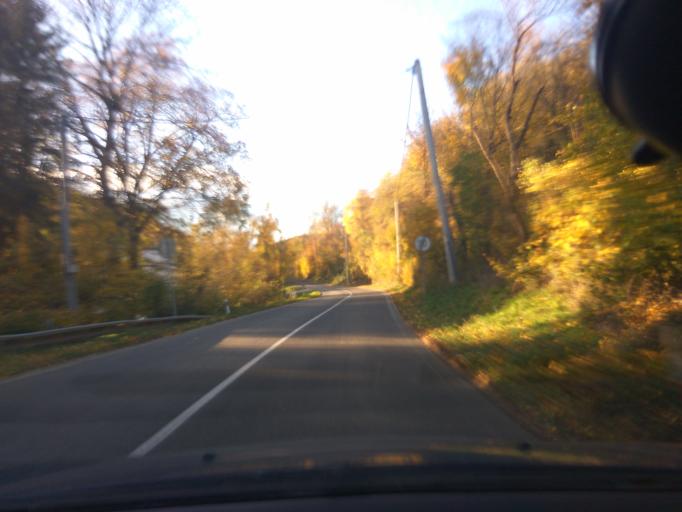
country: SK
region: Trnavsky
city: Vrbove
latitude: 48.6439
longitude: 17.6397
